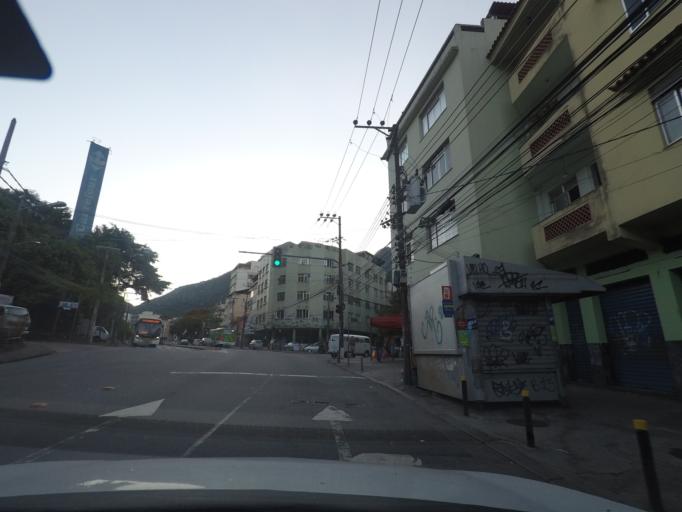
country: BR
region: Rio de Janeiro
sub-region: Rio De Janeiro
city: Rio de Janeiro
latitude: -22.9411
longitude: -43.2519
